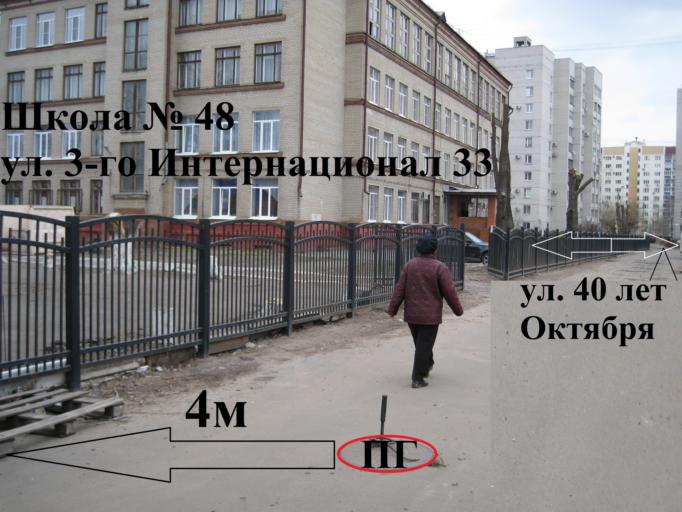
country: RU
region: Voronezj
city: Voronezh
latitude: 51.6698
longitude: 39.1797
